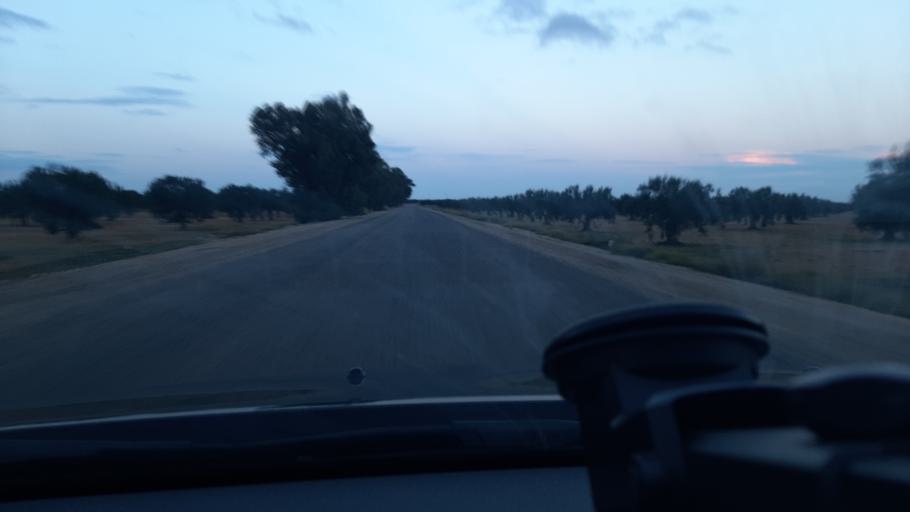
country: TN
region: Al Mahdiyah
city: Shurban
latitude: 34.9799
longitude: 10.3825
